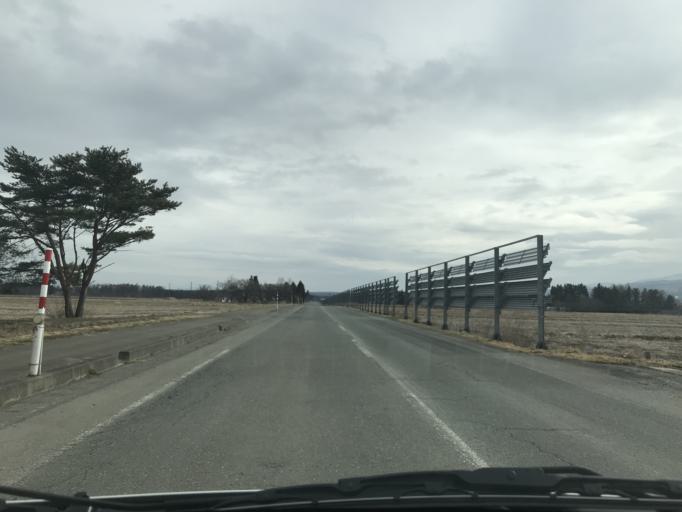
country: JP
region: Iwate
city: Hanamaki
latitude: 39.3378
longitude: 140.9933
